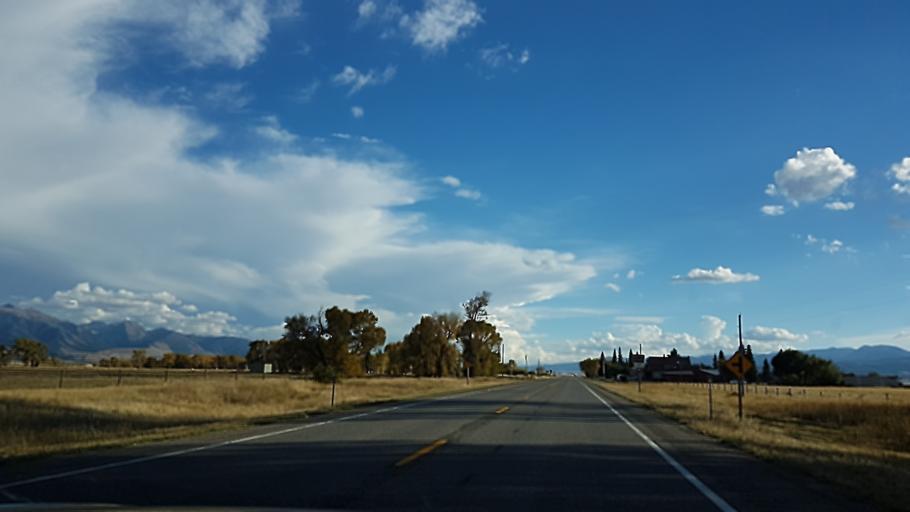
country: US
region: Montana
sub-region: Madison County
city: Virginia City
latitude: 45.2056
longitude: -111.6788
